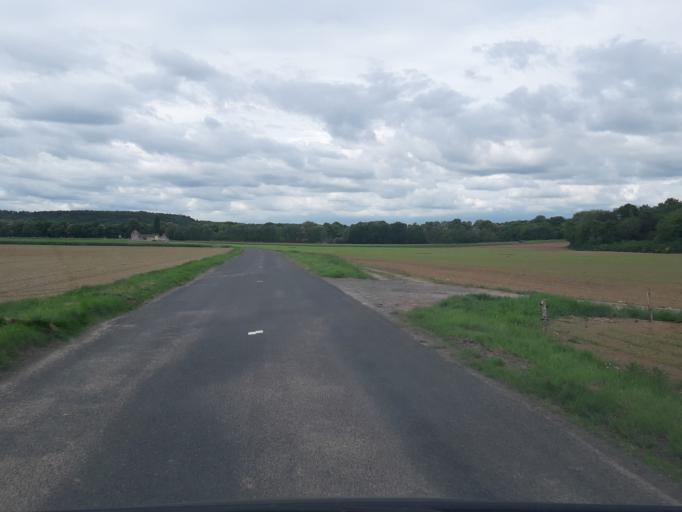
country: FR
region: Ile-de-France
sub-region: Departement de l'Essonne
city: Boissy-le-Cutte
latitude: 48.4188
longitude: 2.2837
